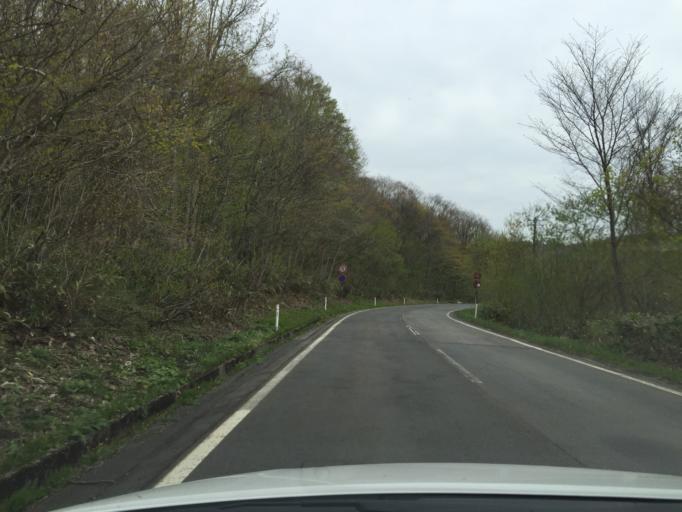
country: JP
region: Fukushima
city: Inawashiro
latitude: 37.5985
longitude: 140.2429
